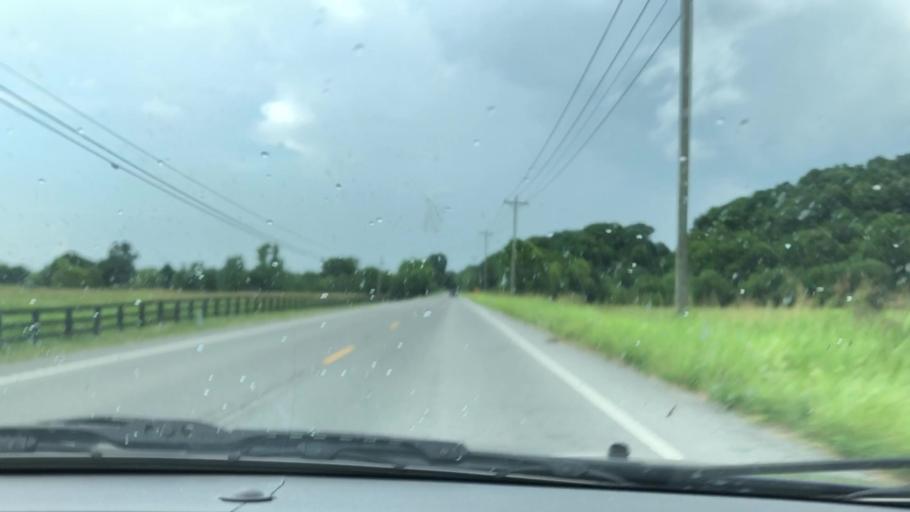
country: US
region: Tennessee
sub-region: Williamson County
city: Thompson's Station
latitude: 35.8408
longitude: -86.9632
